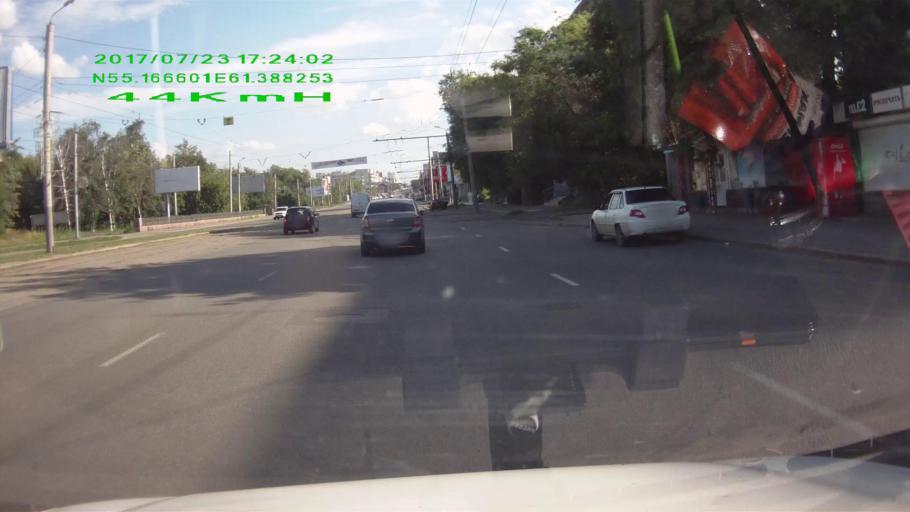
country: RU
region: Chelyabinsk
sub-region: Gorod Chelyabinsk
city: Chelyabinsk
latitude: 55.1664
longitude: 61.3883
